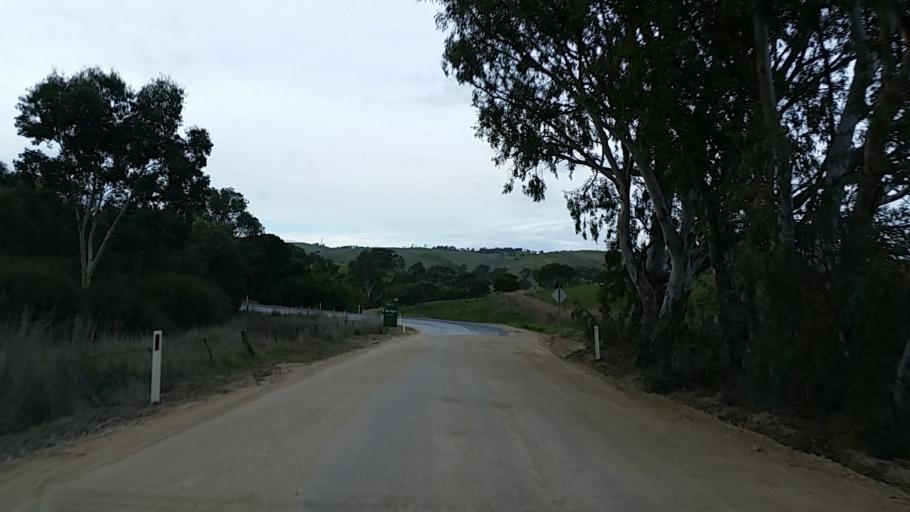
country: AU
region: South Australia
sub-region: Mount Barker
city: Nairne
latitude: -34.9528
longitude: 139.0142
